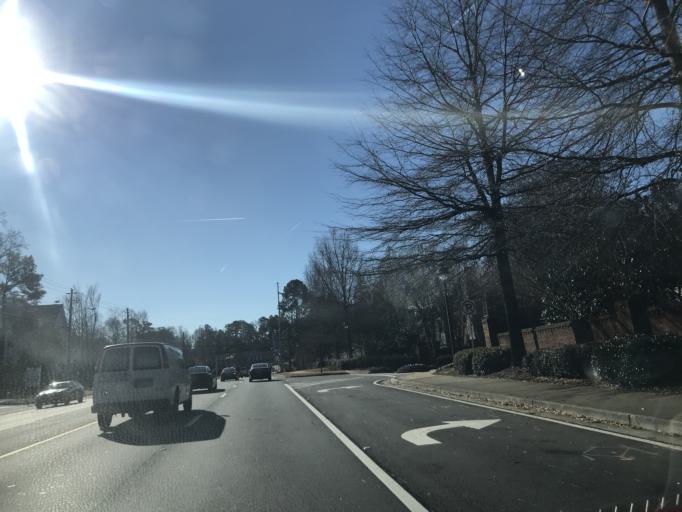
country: US
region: Georgia
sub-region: Fulton County
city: Sandy Springs
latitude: 33.9047
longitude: -84.3788
